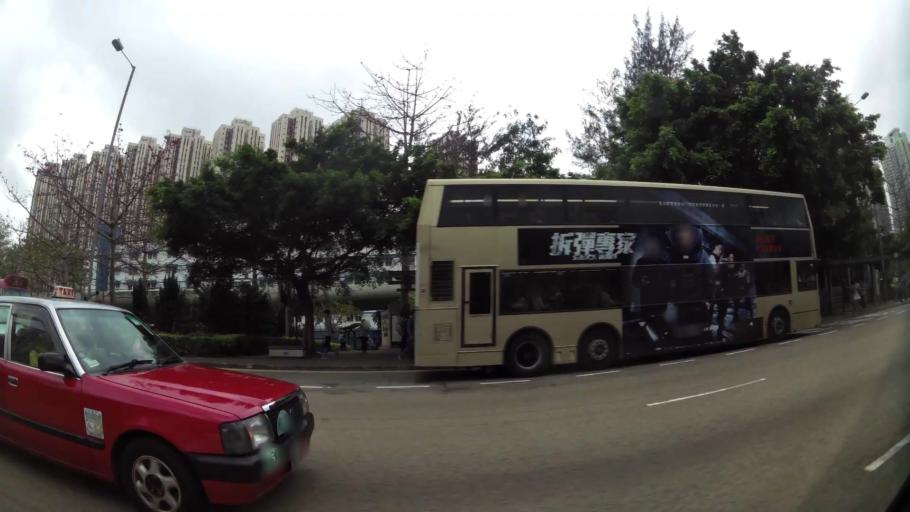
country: HK
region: Kowloon City
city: Kowloon
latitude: 22.3325
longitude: 114.2072
